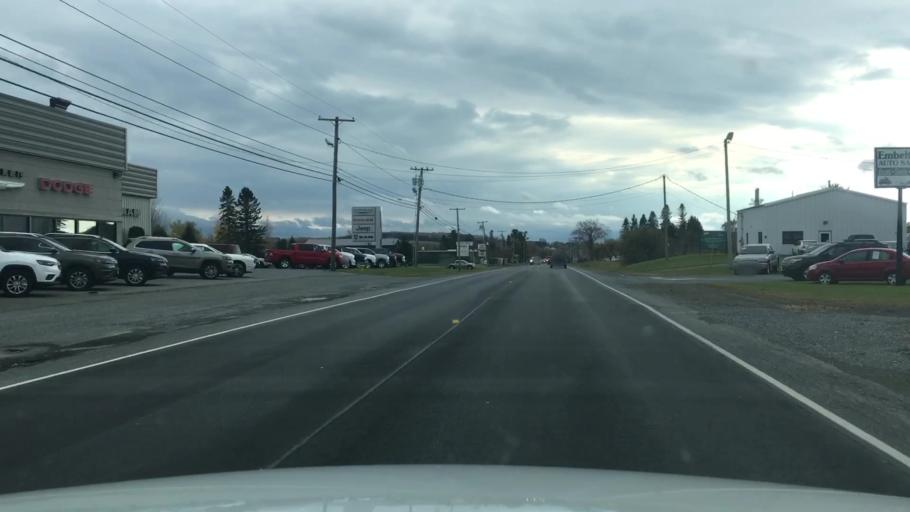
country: US
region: Maine
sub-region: Aroostook County
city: Presque Isle
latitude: 46.6583
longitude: -68.0070
